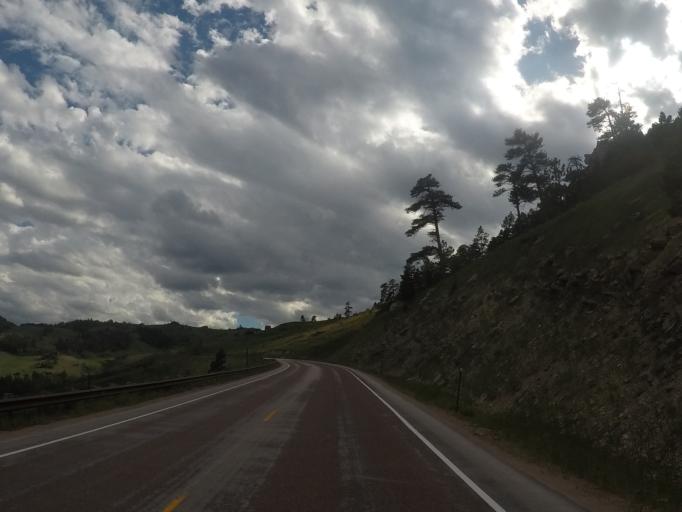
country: US
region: Wyoming
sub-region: Sheridan County
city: Sheridan
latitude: 44.8071
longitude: -107.3494
